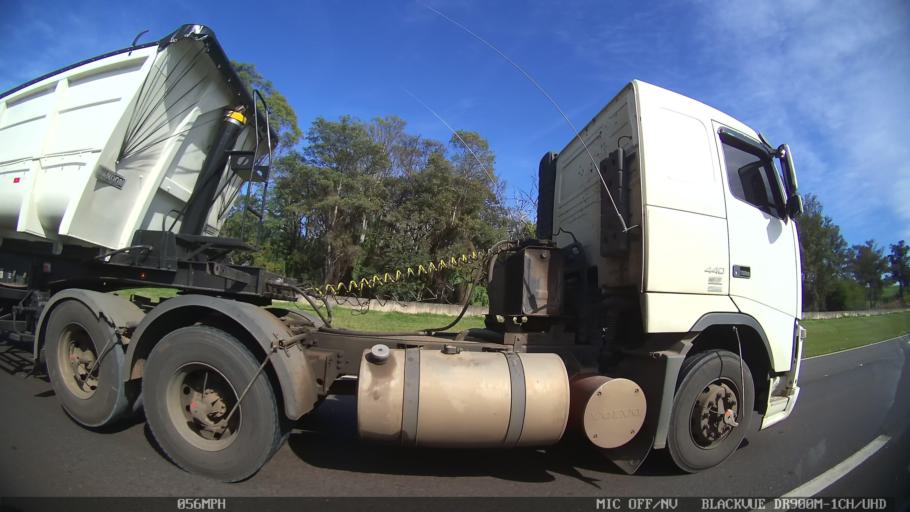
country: BR
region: Sao Paulo
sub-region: Araras
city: Araras
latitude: -22.3919
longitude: -47.3927
